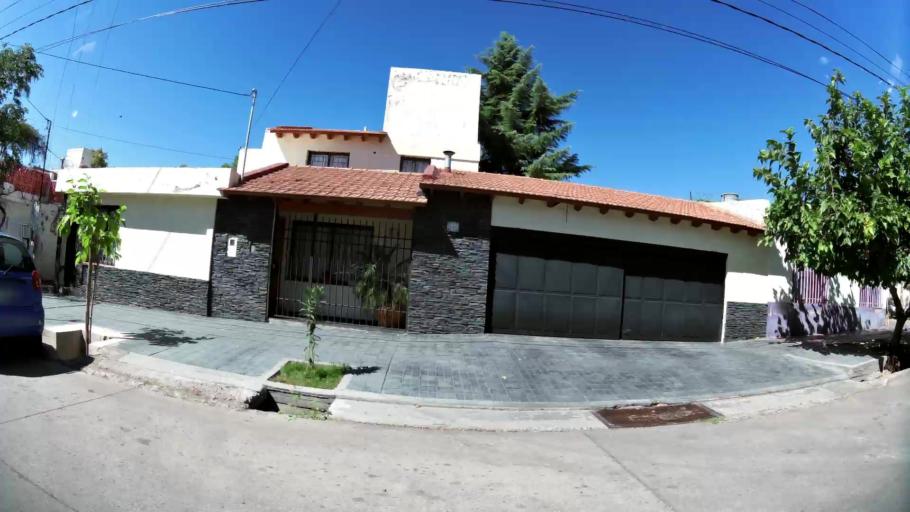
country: AR
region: Mendoza
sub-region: Departamento de Godoy Cruz
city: Godoy Cruz
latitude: -32.9068
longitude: -68.8629
